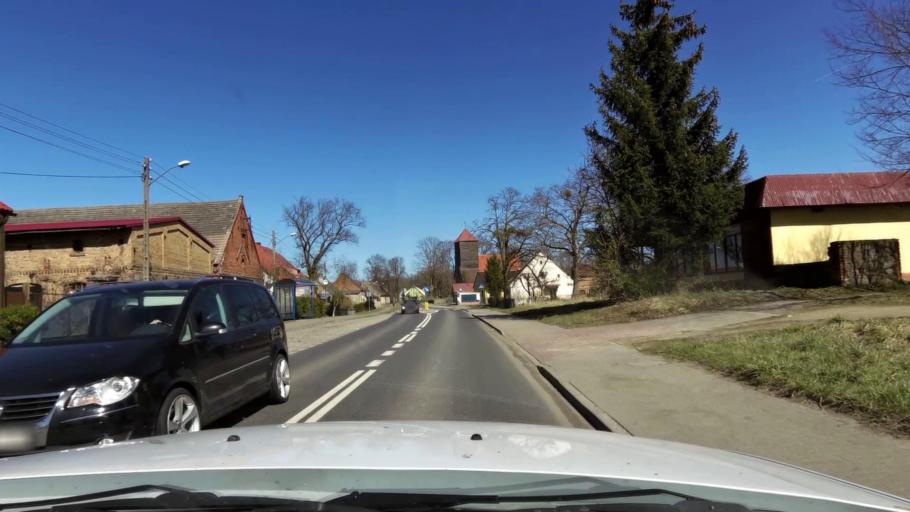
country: PL
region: West Pomeranian Voivodeship
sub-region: Powiat gryfinski
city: Cedynia
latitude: 52.8854
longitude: 14.2860
